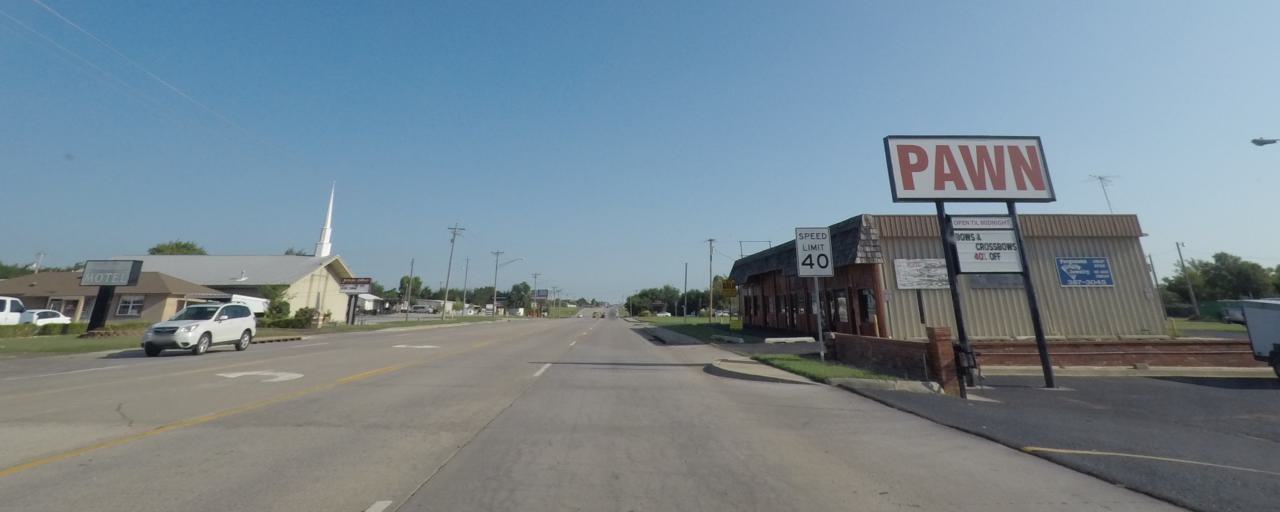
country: US
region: Oklahoma
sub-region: McClain County
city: Newcastle
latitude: 35.2588
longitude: -97.6001
